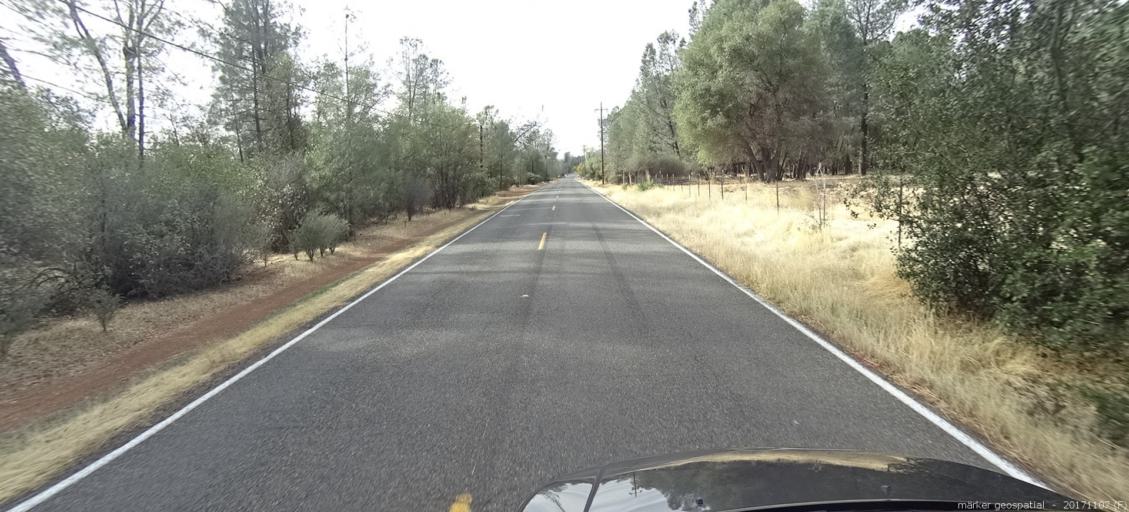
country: US
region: California
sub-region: Shasta County
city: Shasta
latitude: 40.4739
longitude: -122.4588
